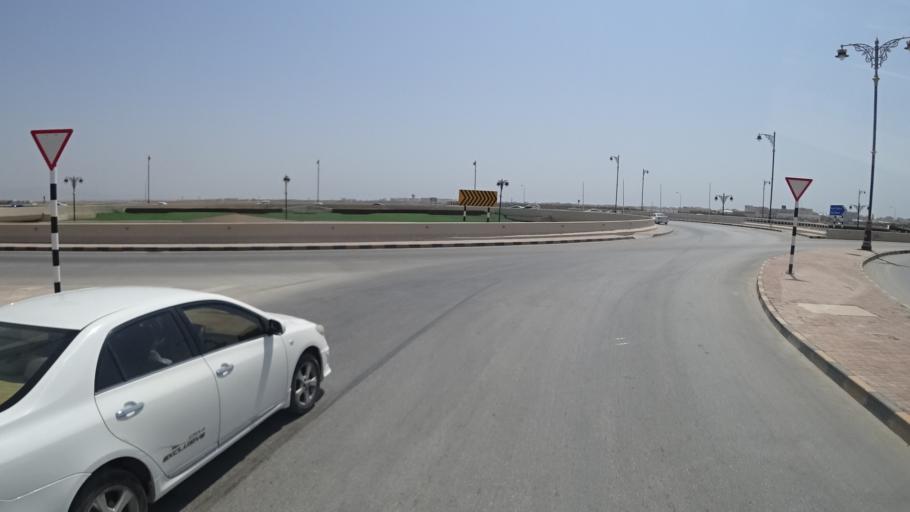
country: OM
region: Zufar
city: Salalah
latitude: 17.0324
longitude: 54.0588
